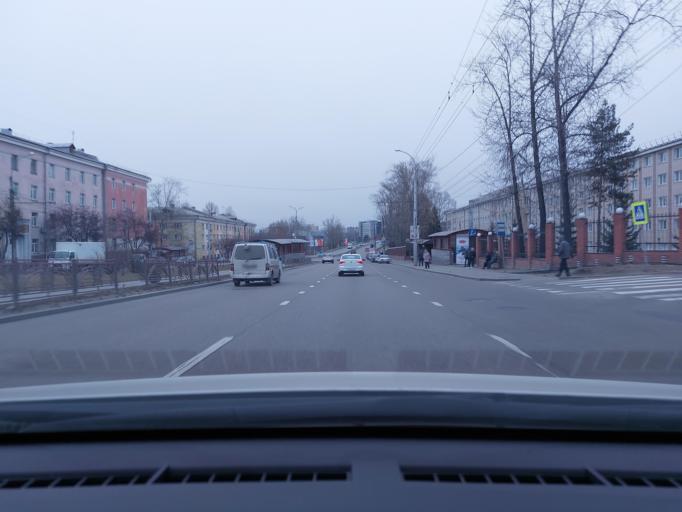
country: RU
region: Irkutsk
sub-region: Irkutskiy Rayon
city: Irkutsk
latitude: 52.2583
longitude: 104.2621
